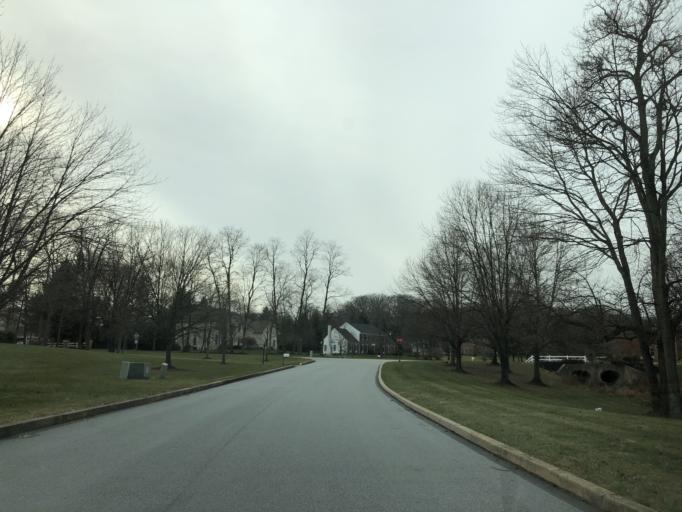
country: US
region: Pennsylvania
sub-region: Chester County
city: Exton
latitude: 40.0352
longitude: -75.6449
